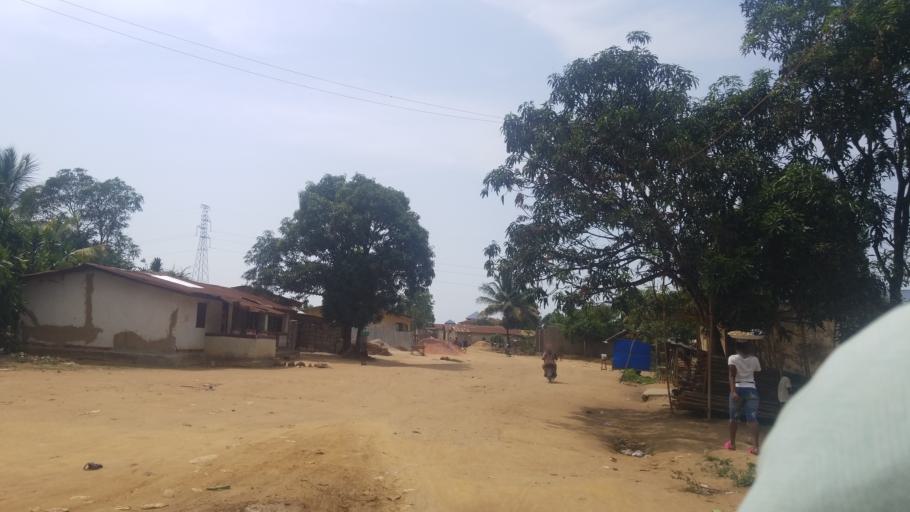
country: SL
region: Western Area
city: Waterloo
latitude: 8.3247
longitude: -13.0477
